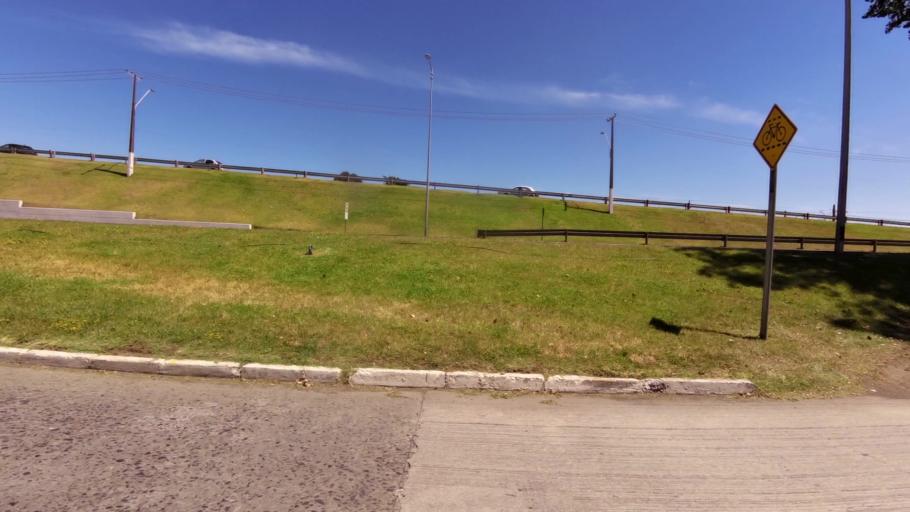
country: CL
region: Biobio
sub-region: Provincia de Concepcion
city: Talcahuano
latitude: -36.7644
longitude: -73.0864
